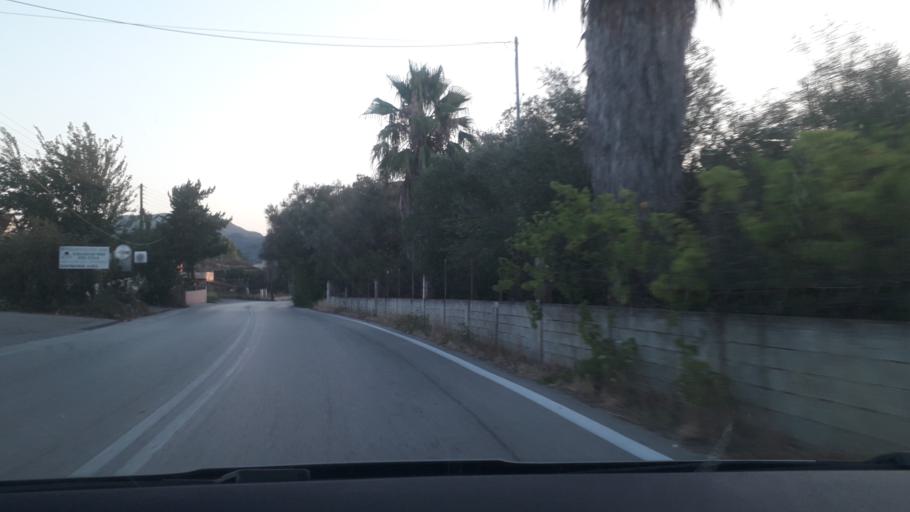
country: GR
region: Ionian Islands
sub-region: Nomos Kerkyras
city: Agios Matthaios
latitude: 39.4720
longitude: 19.9113
